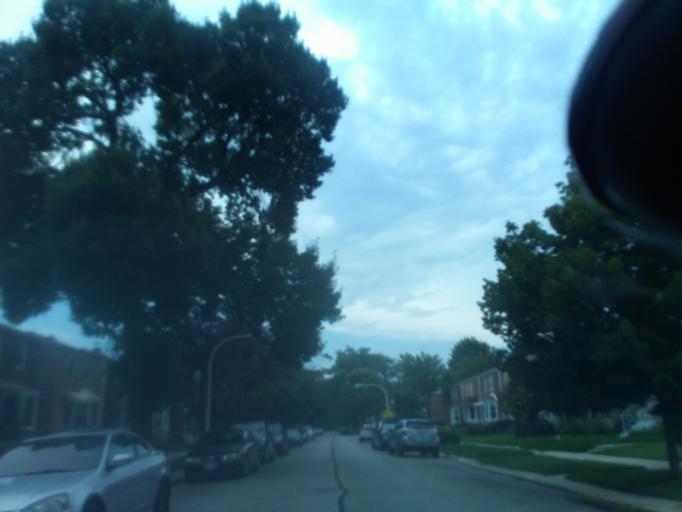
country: US
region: Illinois
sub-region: Cook County
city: Lincolnwood
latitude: 41.9964
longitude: -87.7228
